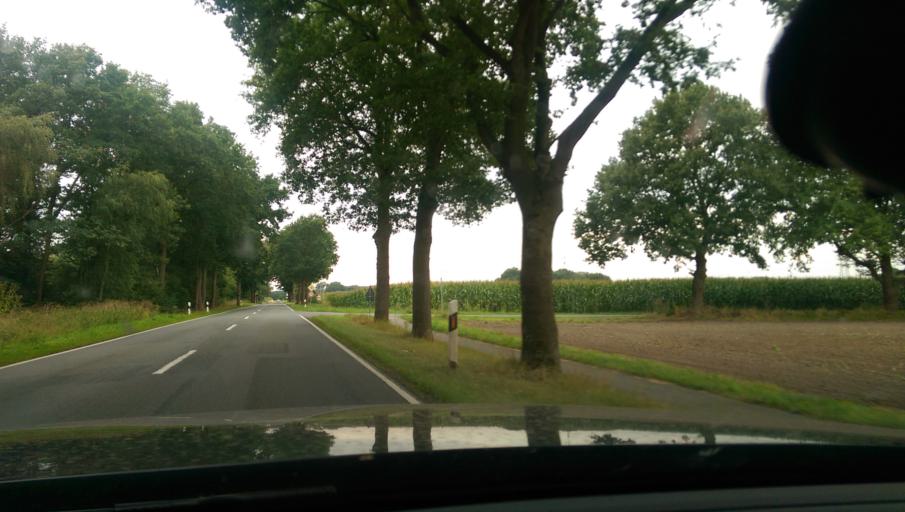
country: DE
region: Lower Saxony
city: Rehburg-Loccum
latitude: 52.4665
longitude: 9.1821
